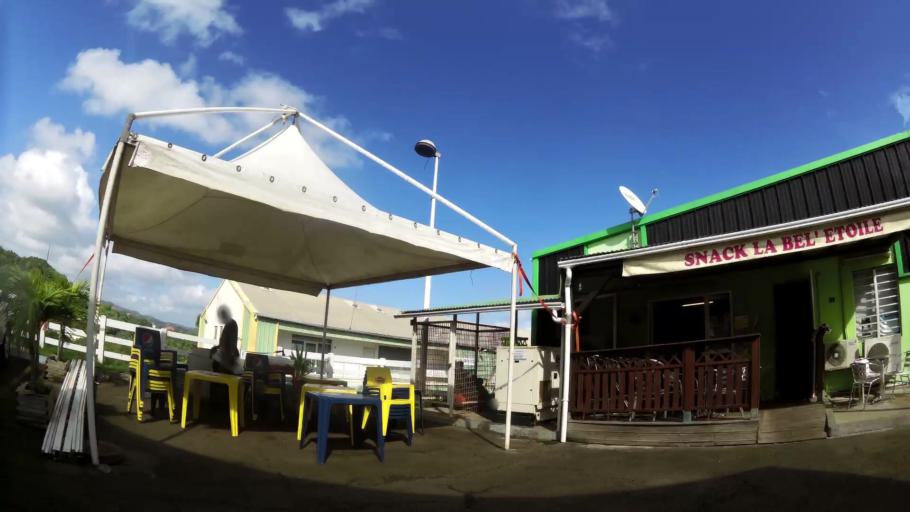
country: MQ
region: Martinique
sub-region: Martinique
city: Sainte-Marie
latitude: 14.7746
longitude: -60.9870
